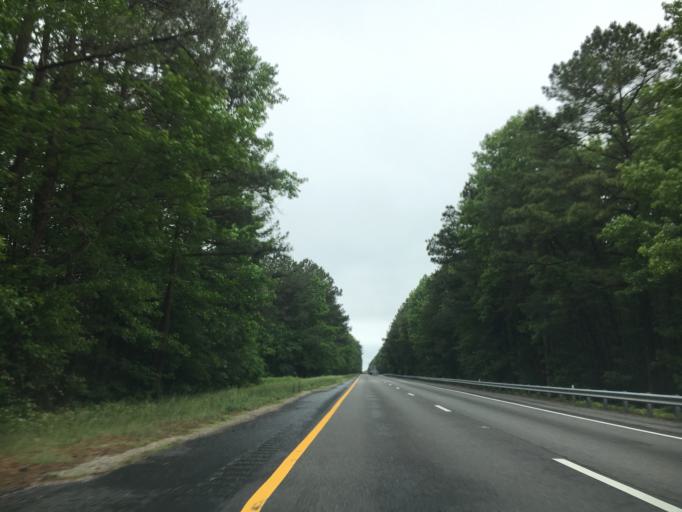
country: US
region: Virginia
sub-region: Dinwiddie County
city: Dinwiddie
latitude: 37.0364
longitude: -77.6305
